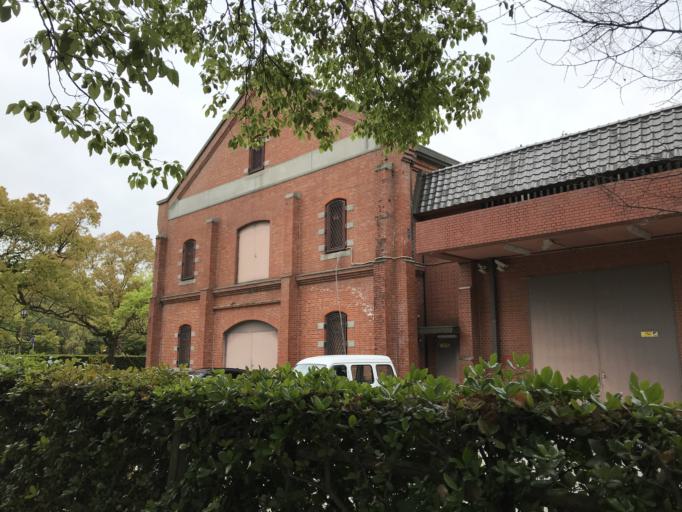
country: JP
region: Hyogo
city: Himeji
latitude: 34.8399
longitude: 134.6963
